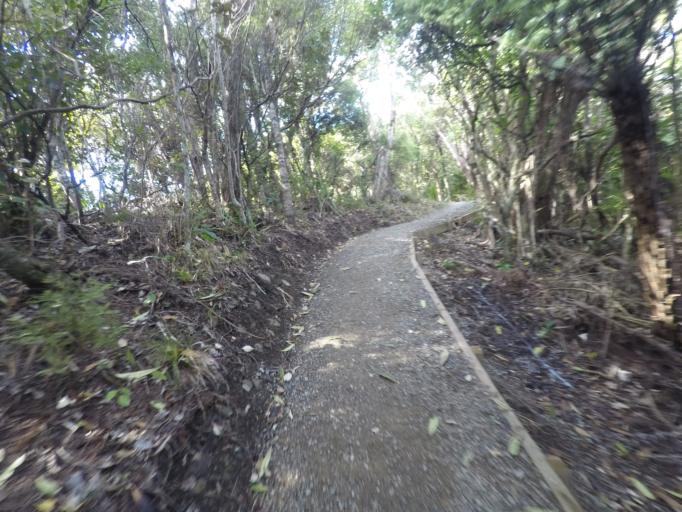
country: NZ
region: Auckland
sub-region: Auckland
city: Titirangi
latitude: -37.0323
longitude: 174.5217
